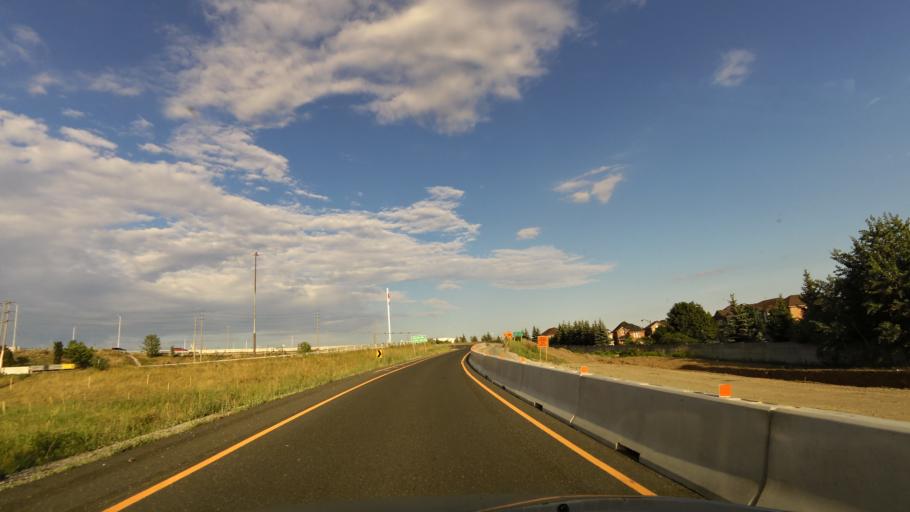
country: CA
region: Ontario
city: Mississauga
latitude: 43.6194
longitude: -79.7095
